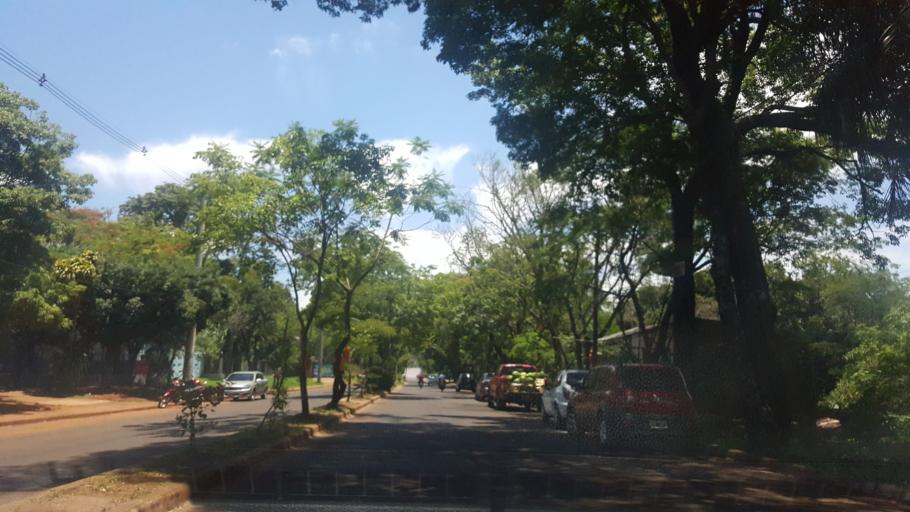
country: AR
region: Misiones
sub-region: Departamento de Capital
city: Posadas
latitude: -27.3566
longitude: -55.9362
